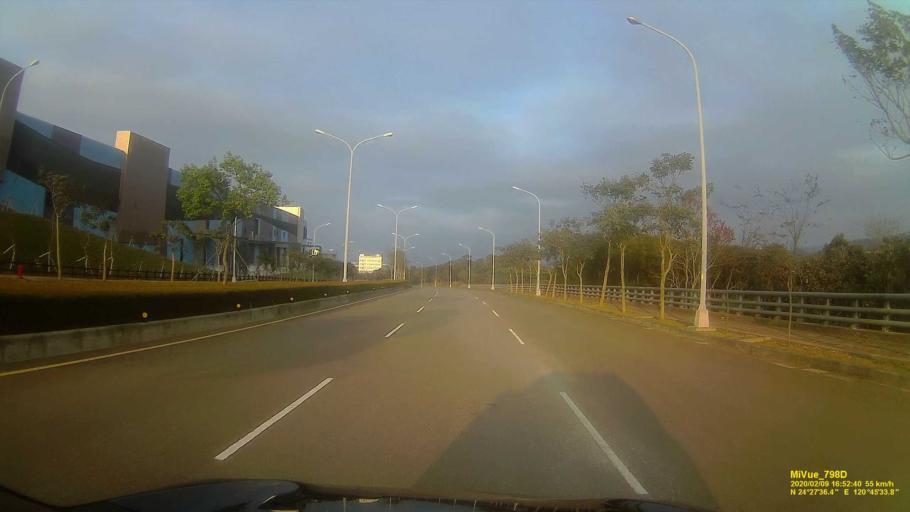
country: TW
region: Taiwan
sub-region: Miaoli
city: Miaoli
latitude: 24.4602
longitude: 120.7596
